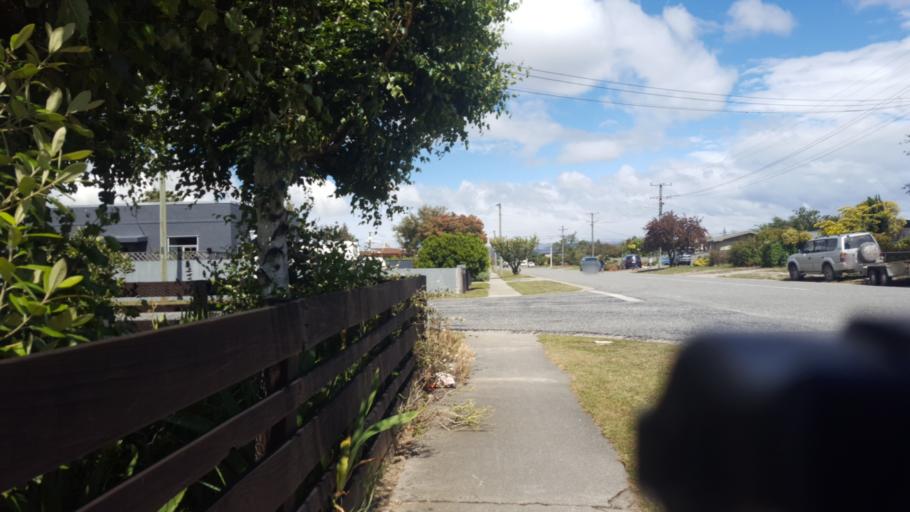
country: NZ
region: Otago
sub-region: Queenstown-Lakes District
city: Wanaka
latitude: -45.1896
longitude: 169.3265
